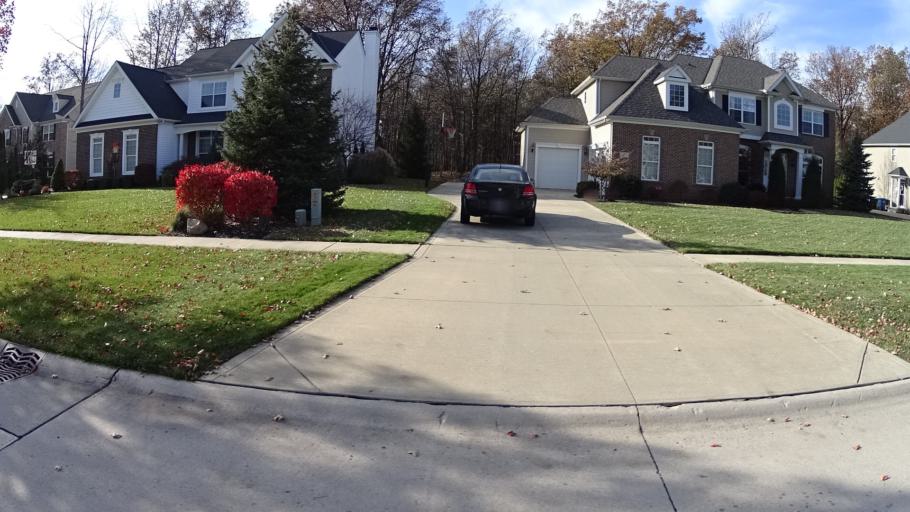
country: US
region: Ohio
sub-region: Lorain County
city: Avon Lake
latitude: 41.4961
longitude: -81.9836
